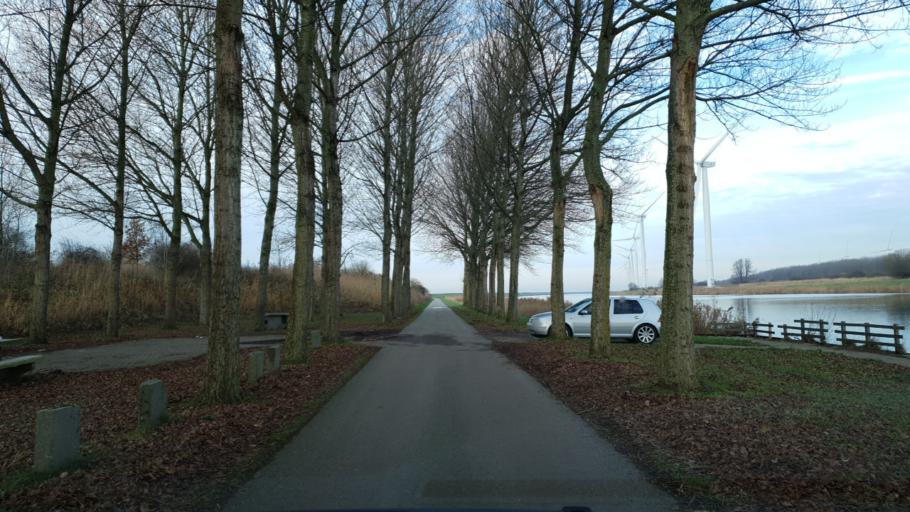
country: NL
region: North Brabant
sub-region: Gemeente Woensdrecht
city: Woensdrecht
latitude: 51.4337
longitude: 4.2272
